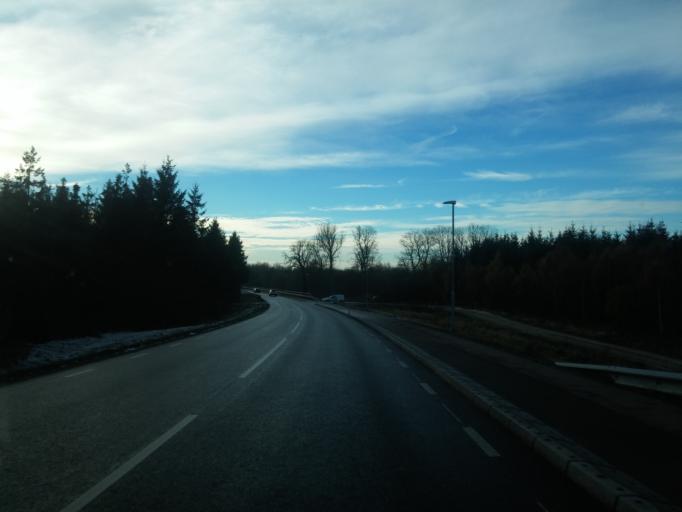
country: SE
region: Skane
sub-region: Angelholms Kommun
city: Strovelstorp
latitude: 56.2153
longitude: 12.7989
